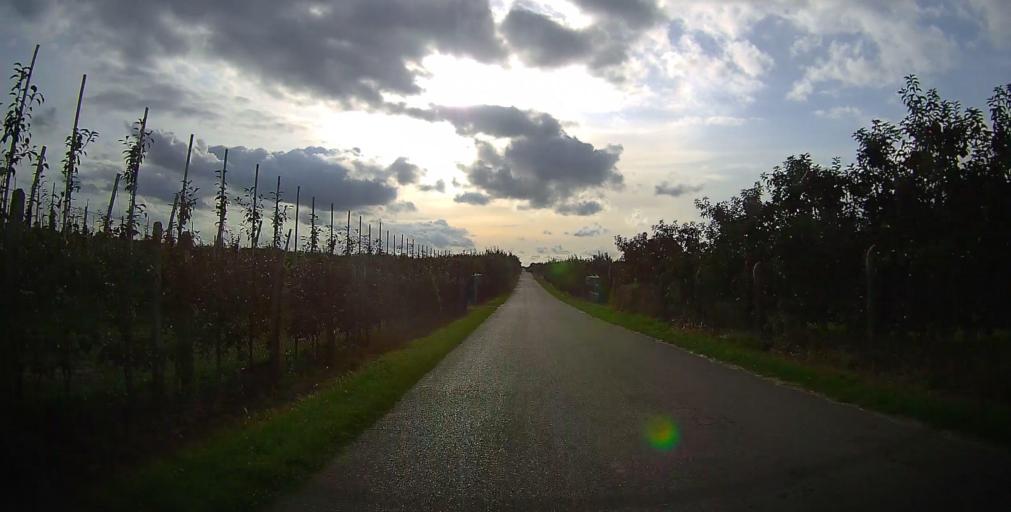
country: PL
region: Masovian Voivodeship
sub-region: Powiat grojecki
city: Jasieniec
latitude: 51.7715
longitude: 20.9185
